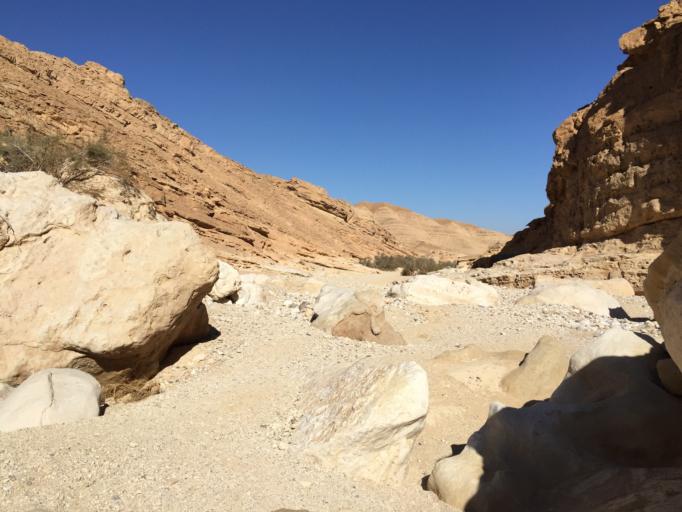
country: IL
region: Southern District
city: Mitzpe Ramon
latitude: 30.6000
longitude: 34.9475
